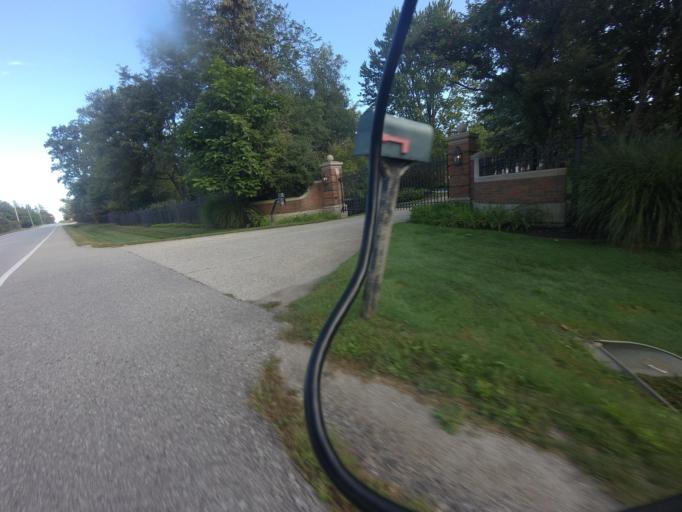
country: CA
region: Ontario
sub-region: Wellington County
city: Guelph
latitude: 43.5779
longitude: -80.3327
